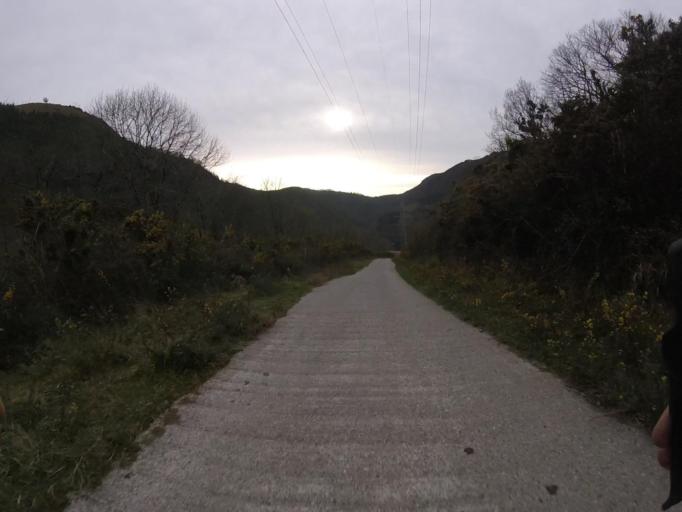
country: ES
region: Navarre
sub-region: Provincia de Navarra
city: Lesaka
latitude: 43.2743
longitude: -1.7595
